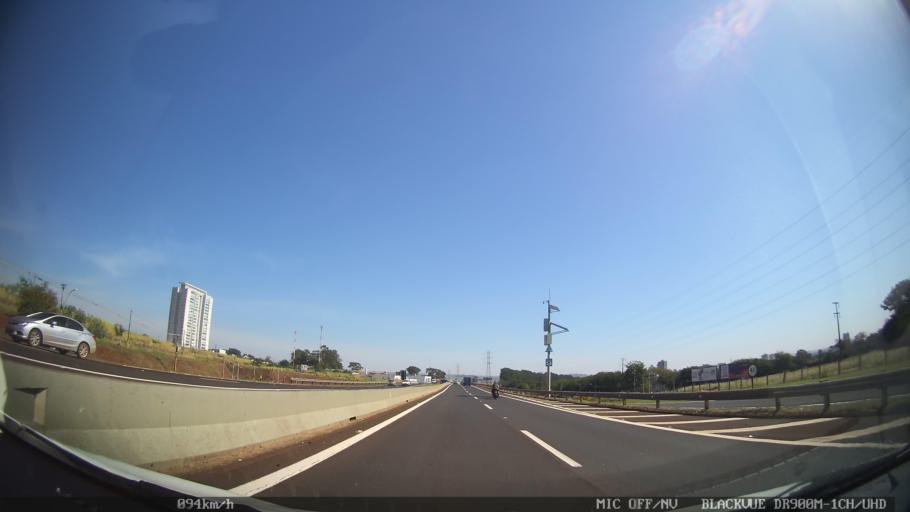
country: BR
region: Sao Paulo
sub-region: Ribeirao Preto
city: Ribeirao Preto
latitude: -21.2244
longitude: -47.8046
